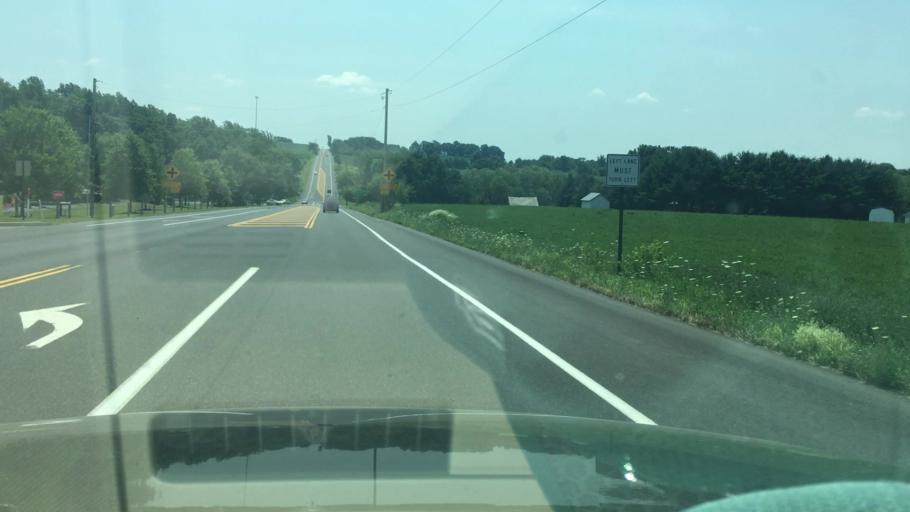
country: US
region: Pennsylvania
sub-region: Carbon County
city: Lehighton
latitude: 40.7100
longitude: -75.7633
